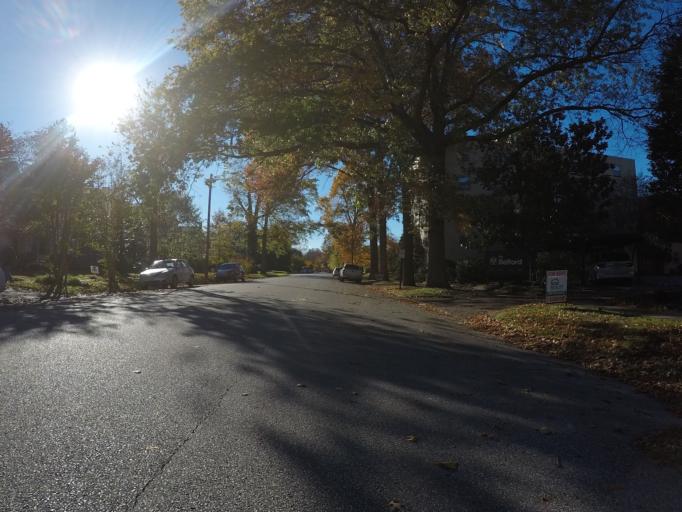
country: US
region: West Virginia
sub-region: Cabell County
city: Huntington
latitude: 38.4104
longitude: -82.4451
